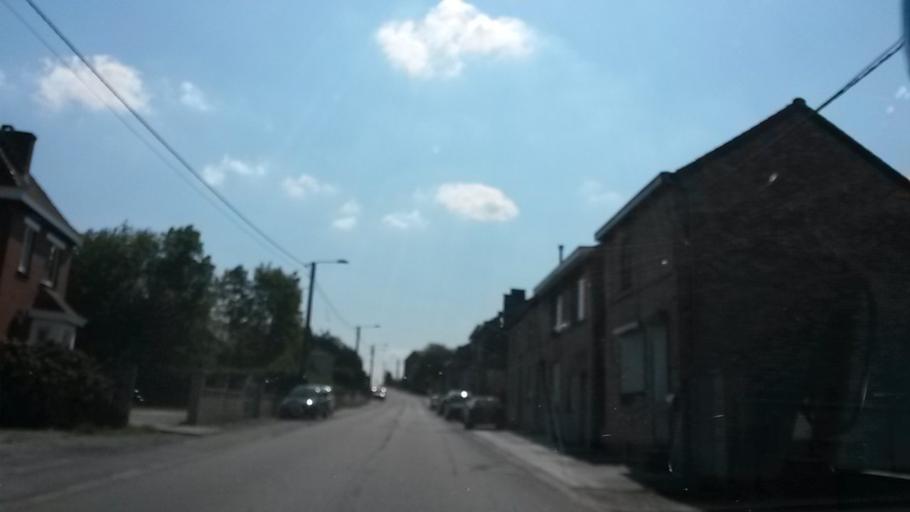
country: BE
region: Wallonia
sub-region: Province du Hainaut
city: Farciennes
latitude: 50.4312
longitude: 4.5058
